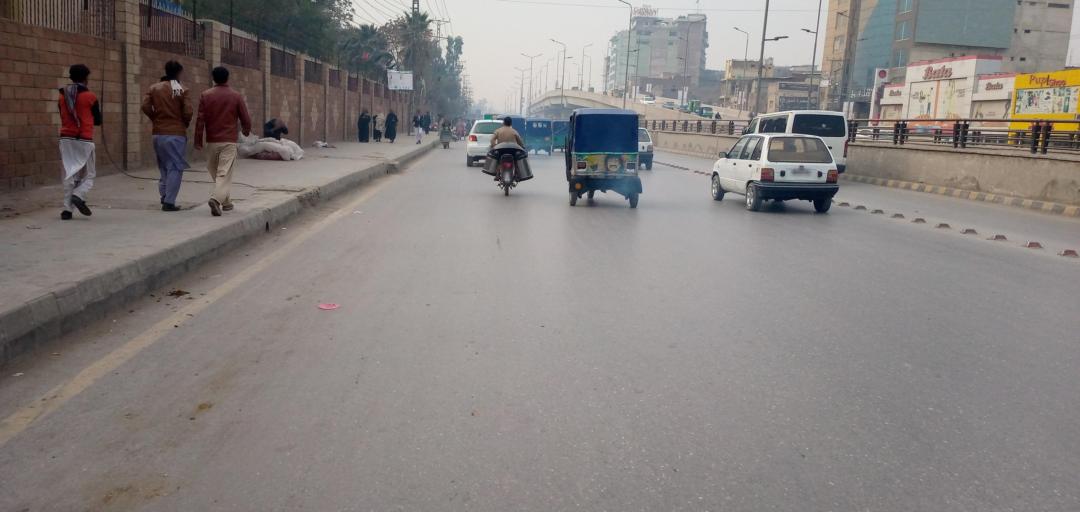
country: PK
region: Khyber Pakhtunkhwa
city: Peshawar
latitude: 34.0146
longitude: 71.5773
